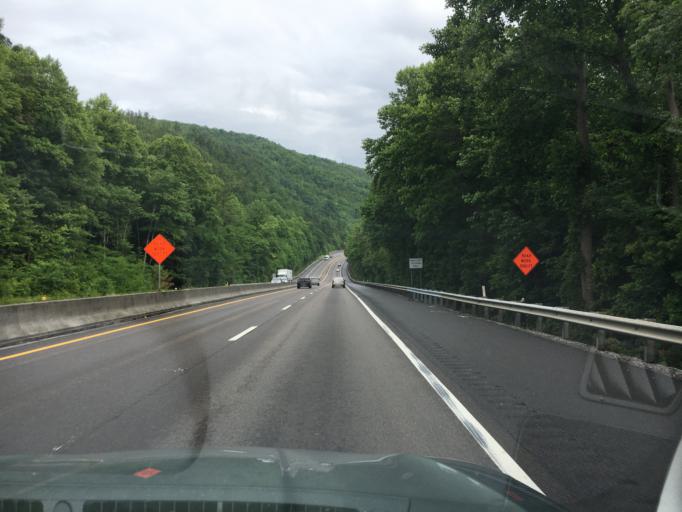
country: US
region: Tennessee
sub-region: Cocke County
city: Newport
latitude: 35.8173
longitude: -83.1796
